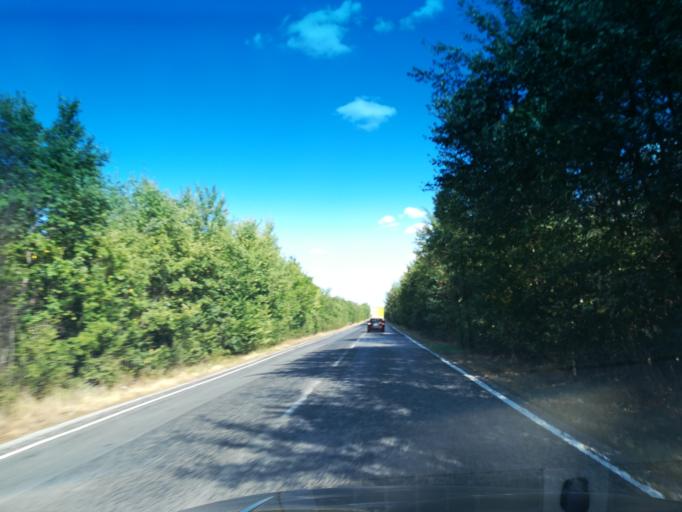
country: BG
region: Khaskovo
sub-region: Obshtina Mineralni Bani
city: Mineralni Bani
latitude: 42.0541
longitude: 25.3125
